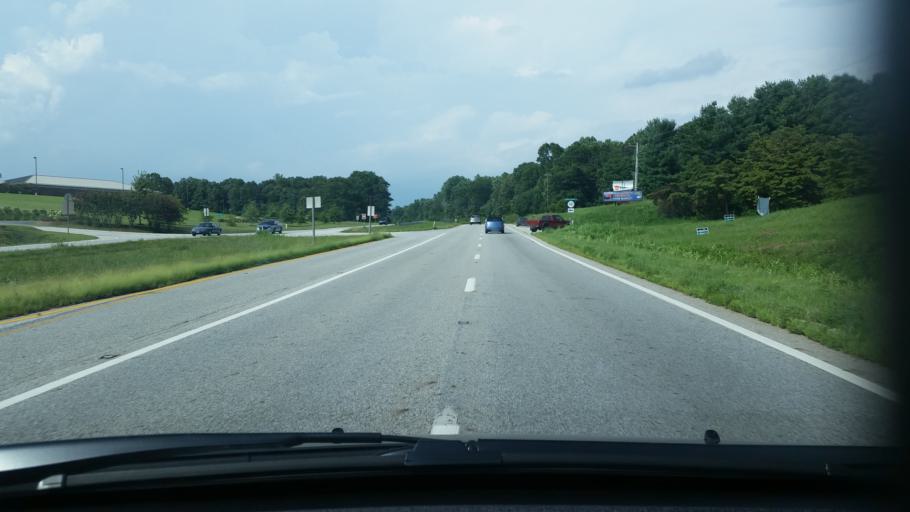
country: US
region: Virginia
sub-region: Nelson County
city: Lovingston
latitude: 37.7309
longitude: -78.8948
